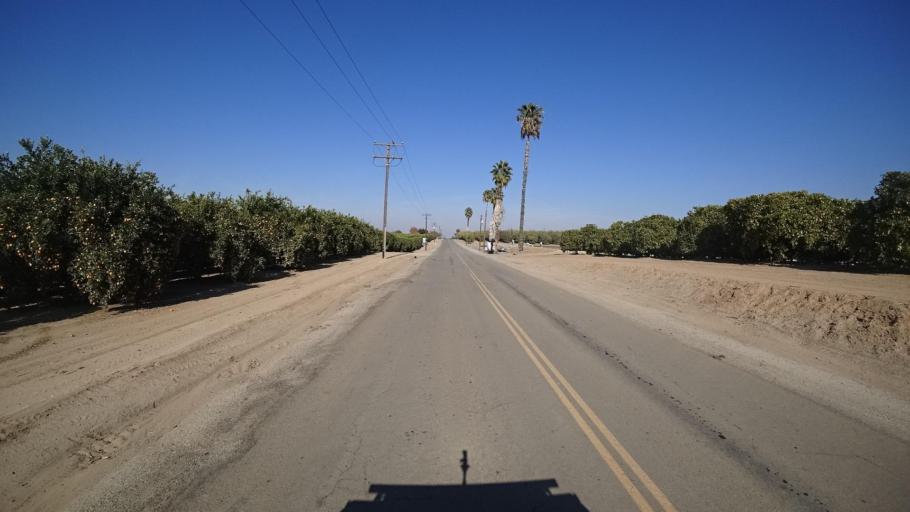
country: US
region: California
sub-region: Tulare County
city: Richgrove
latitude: 35.7141
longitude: -119.1339
